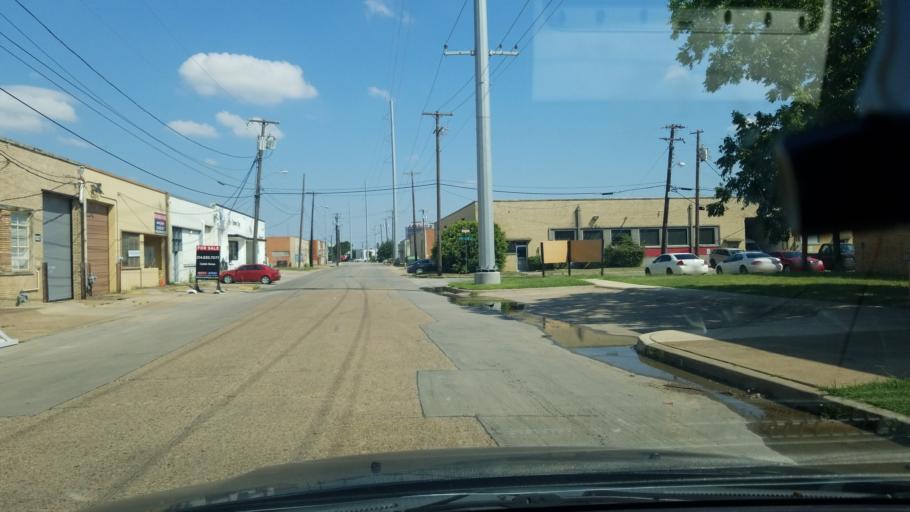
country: US
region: Texas
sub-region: Dallas County
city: Dallas
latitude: 32.7852
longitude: -96.8209
